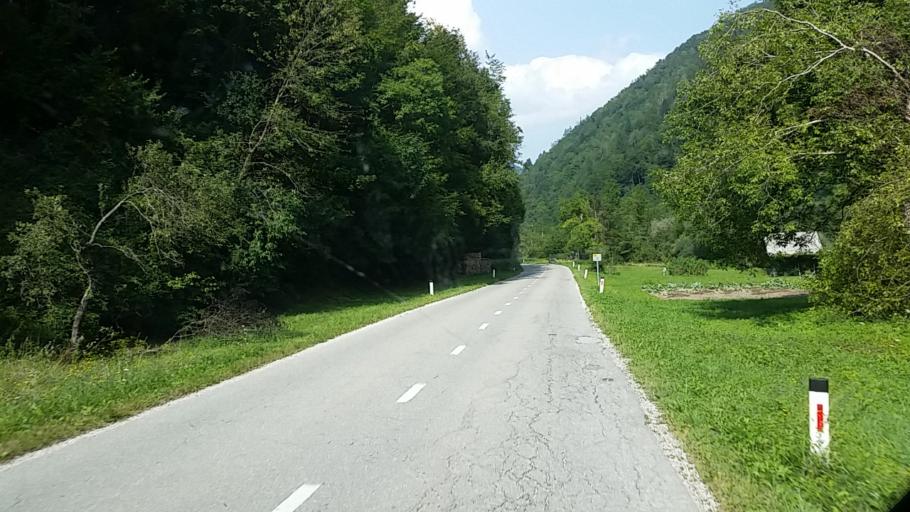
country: SI
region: Cerkno
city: Cerkno
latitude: 46.1812
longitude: 13.9201
